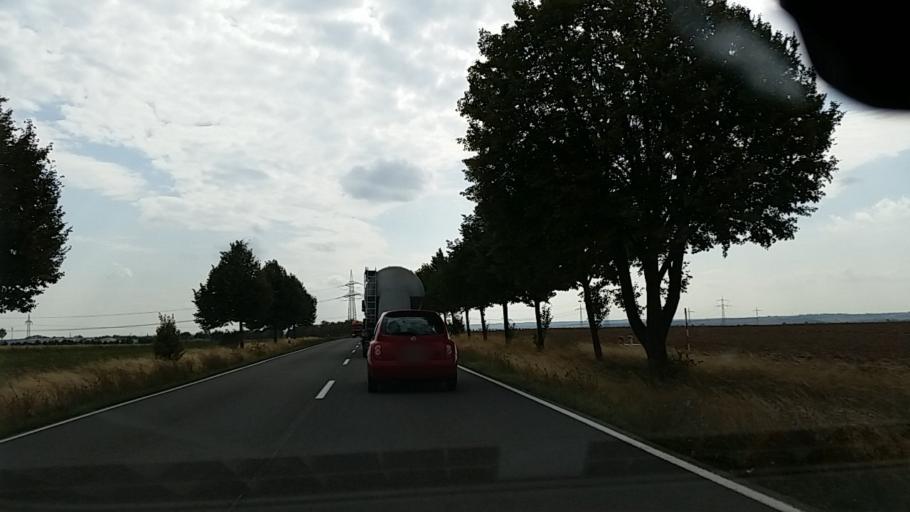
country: DE
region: Saxony-Anhalt
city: Steigra
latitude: 51.3185
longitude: 11.6485
